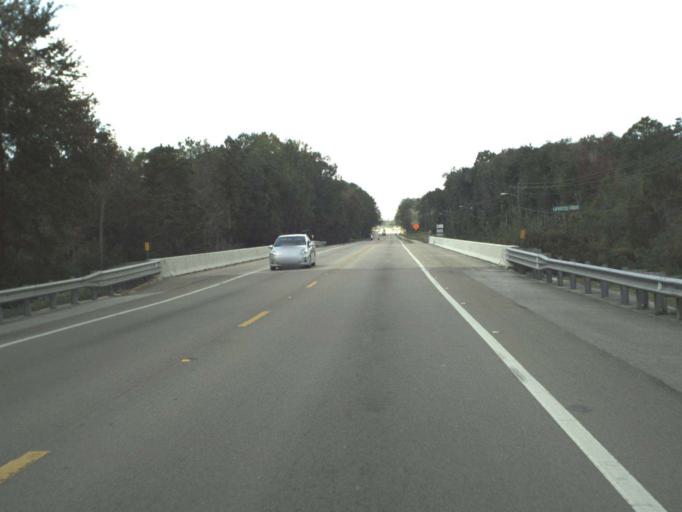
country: US
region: Florida
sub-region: Walton County
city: Freeport
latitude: 30.4929
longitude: -86.1251
